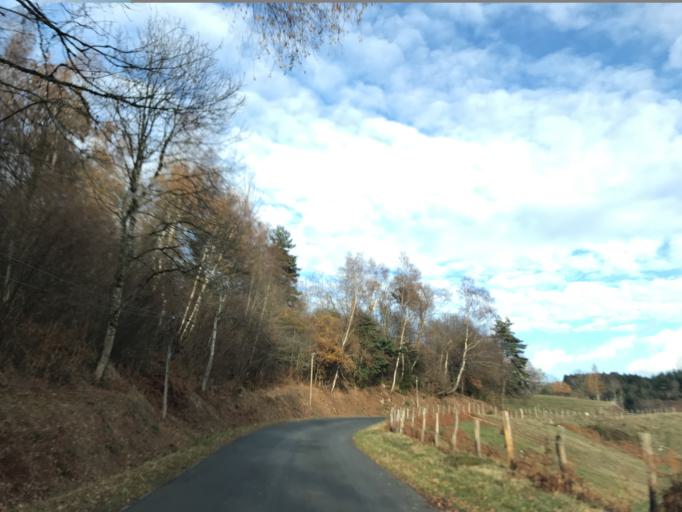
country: FR
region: Auvergne
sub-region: Departement du Puy-de-Dome
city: Celles-sur-Durolle
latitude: 45.7735
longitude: 3.6637
